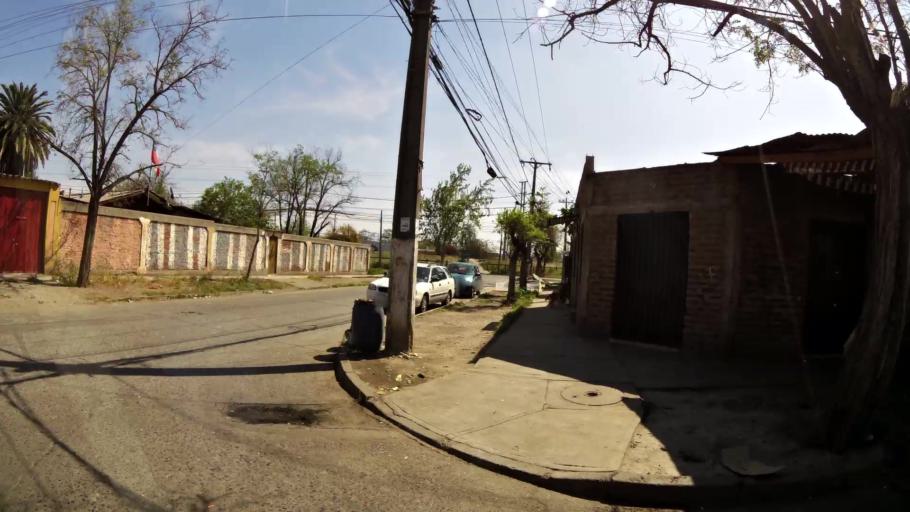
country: CL
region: Santiago Metropolitan
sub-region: Provincia de Santiago
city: Lo Prado
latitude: -33.4140
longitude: -70.6859
